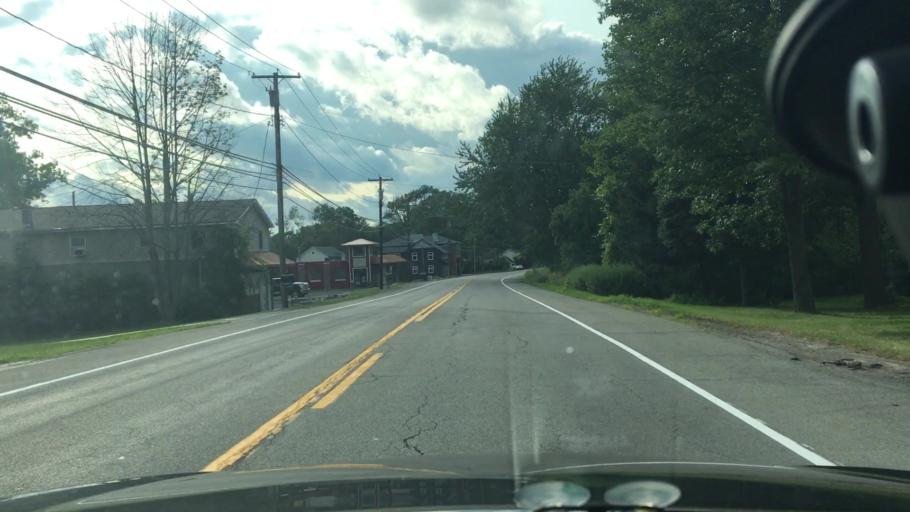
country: US
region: New York
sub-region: Erie County
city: Elma Center
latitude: 42.8185
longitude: -78.6764
